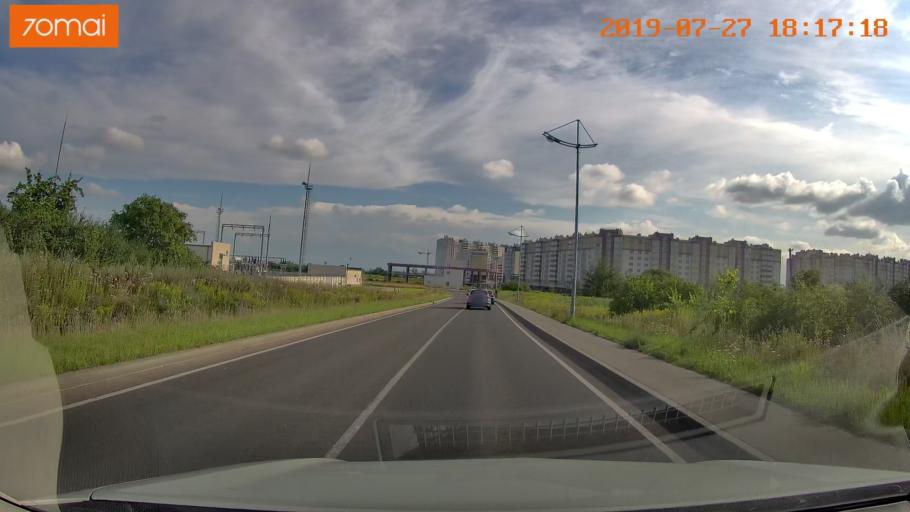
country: RU
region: Kaliningrad
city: Bol'shoe Isakovo
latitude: 54.7165
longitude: 20.5949
